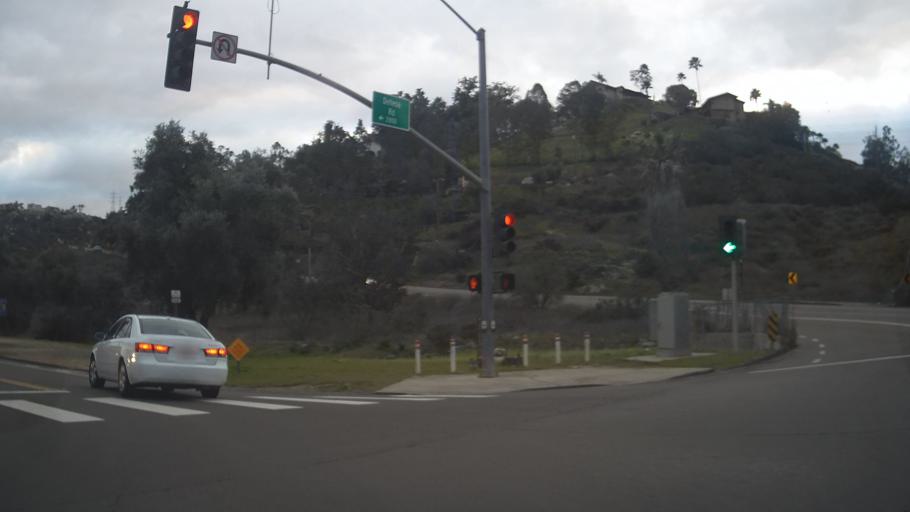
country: US
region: California
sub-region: San Diego County
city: Granite Hills
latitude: 32.7885
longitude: -116.8882
